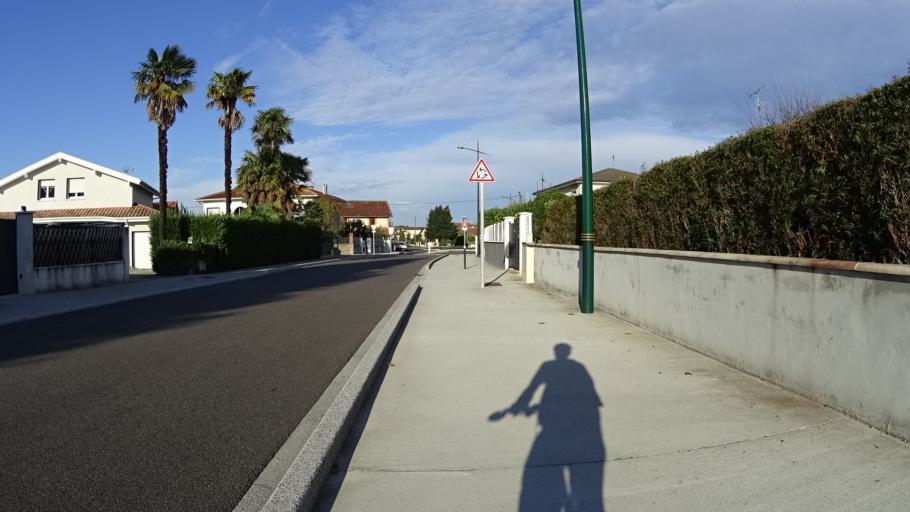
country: FR
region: Aquitaine
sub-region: Departement des Landes
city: Saint-Paul-les-Dax
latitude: 43.7310
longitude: -1.0572
